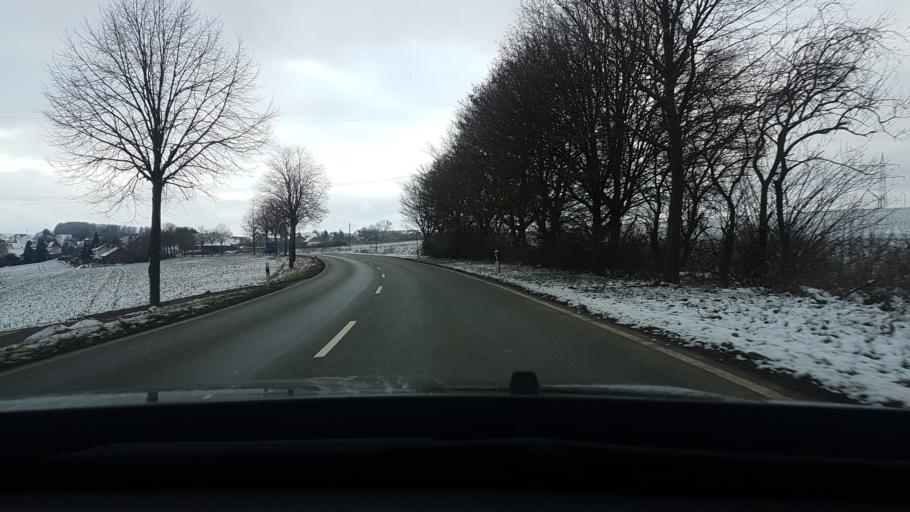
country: DE
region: Hesse
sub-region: Regierungsbezirk Kassel
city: Bad Arolsen
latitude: 51.3916
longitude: 8.9591
